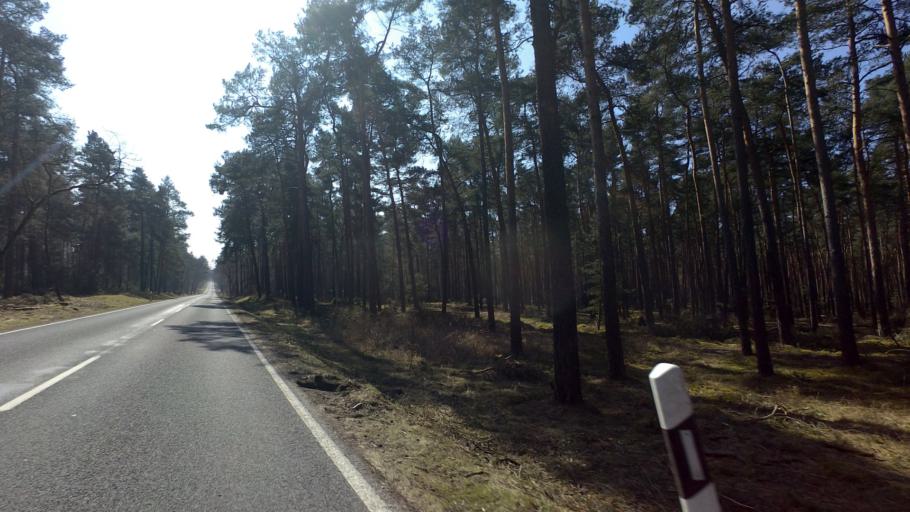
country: DE
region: Saxony-Anhalt
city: Nudersdorf
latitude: 51.9810
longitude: 12.5826
